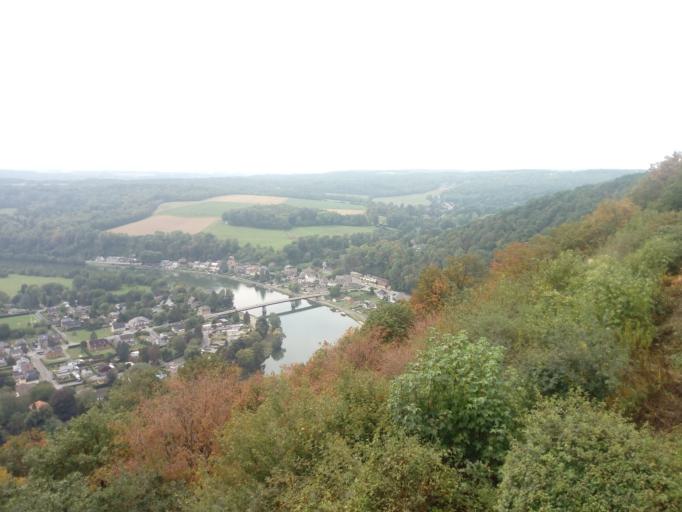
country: BE
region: Wallonia
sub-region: Province de Namur
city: Profondeville
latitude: 50.3541
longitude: 4.8585
